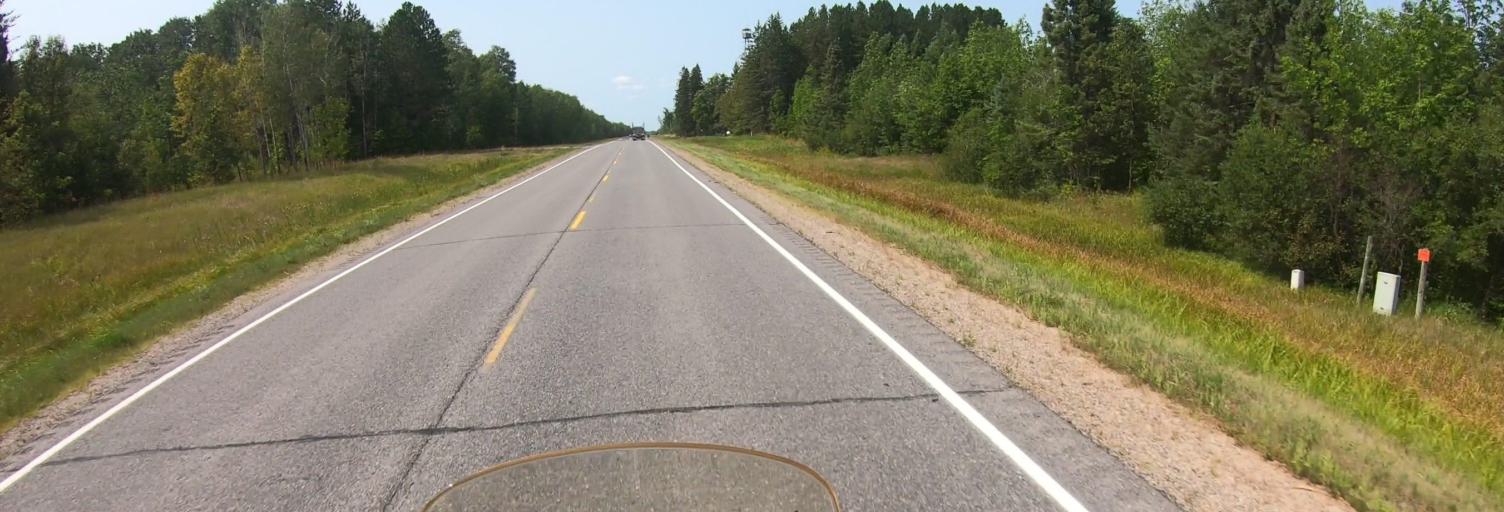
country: US
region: Minnesota
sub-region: Koochiching County
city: International Falls
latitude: 48.5127
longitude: -93.7776
